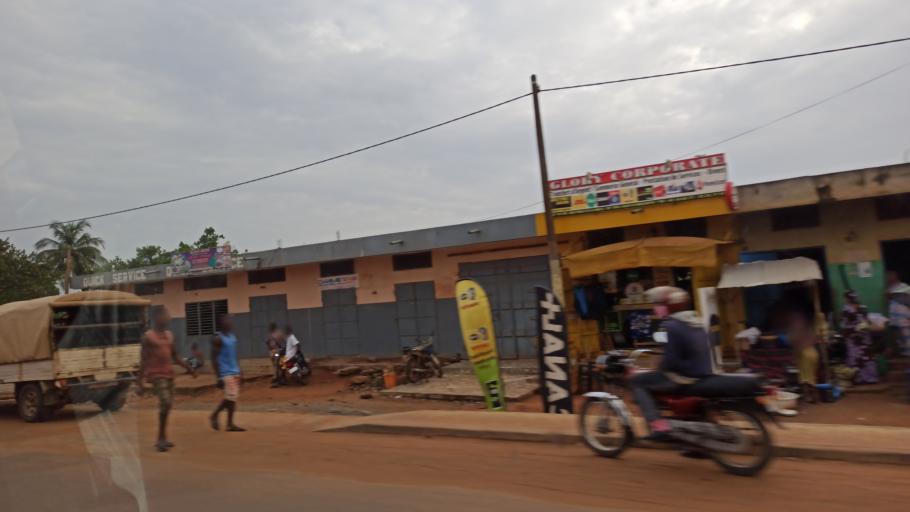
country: BJ
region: Queme
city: Porto-Novo
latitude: 6.5150
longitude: 2.6048
